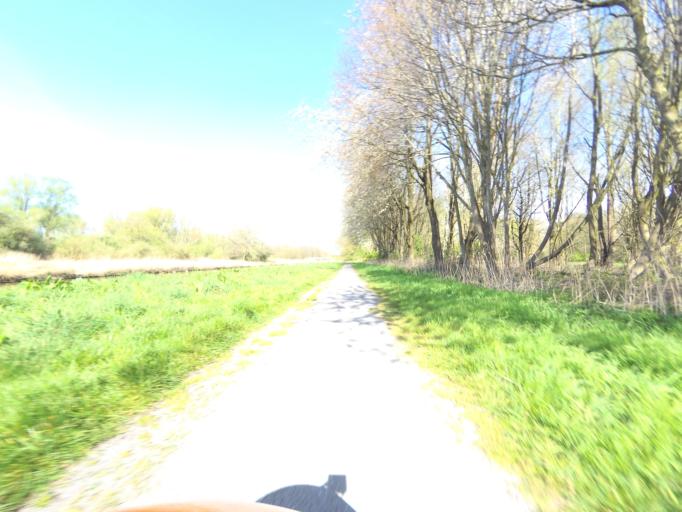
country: NL
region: Flevoland
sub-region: Gemeente Lelystad
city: Lelystad
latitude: 52.4479
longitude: 5.5546
